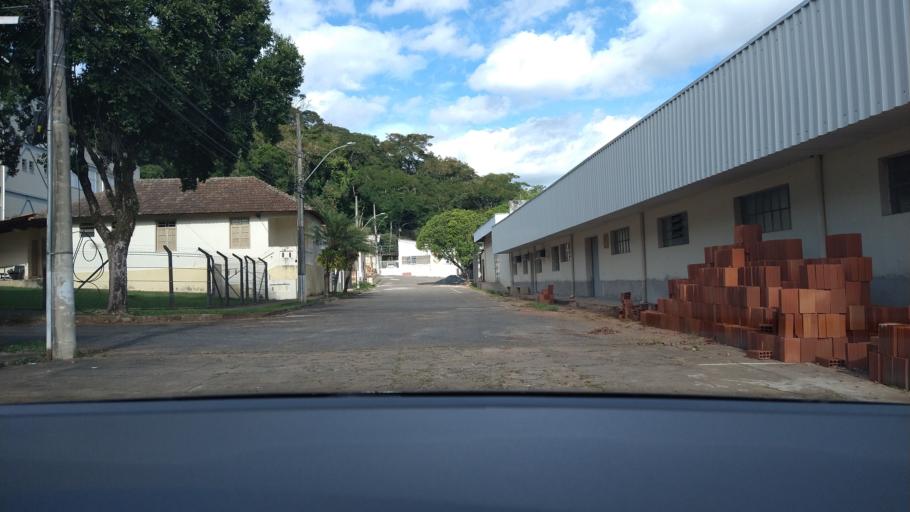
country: BR
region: Minas Gerais
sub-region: Vicosa
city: Vicosa
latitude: -20.7628
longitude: -42.8662
